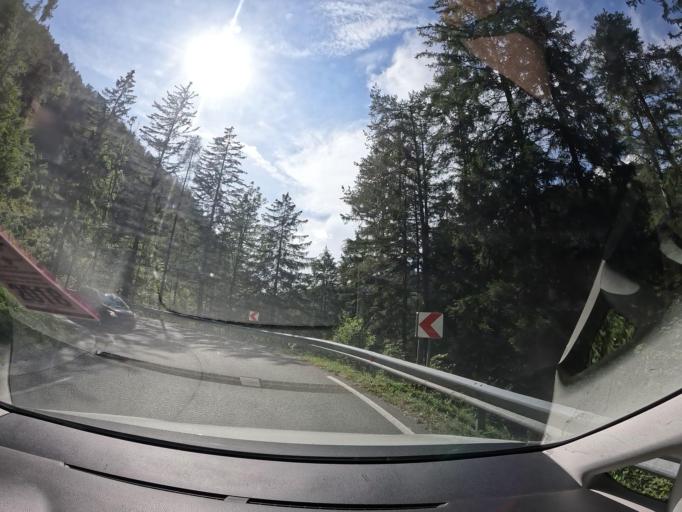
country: AT
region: Carinthia
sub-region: Politischer Bezirk Klagenfurt Land
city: Ludmannsdorf
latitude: 46.5241
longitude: 14.0944
